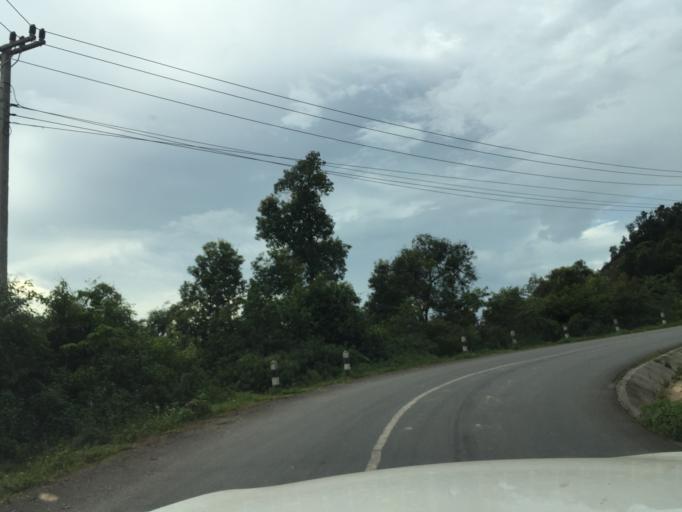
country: LA
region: Phongsali
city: Phongsali
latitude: 21.3109
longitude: 102.0485
